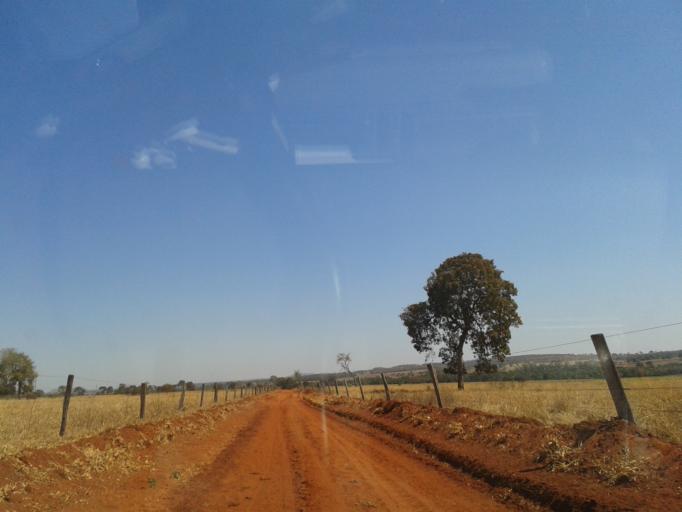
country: BR
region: Minas Gerais
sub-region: Santa Vitoria
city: Santa Vitoria
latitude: -19.0772
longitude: -50.0641
